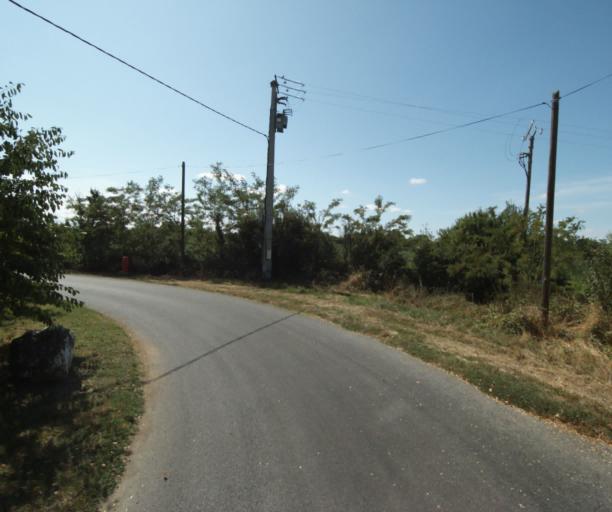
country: FR
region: Midi-Pyrenees
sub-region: Departement de la Haute-Garonne
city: Revel
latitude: 43.4997
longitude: 2.0058
